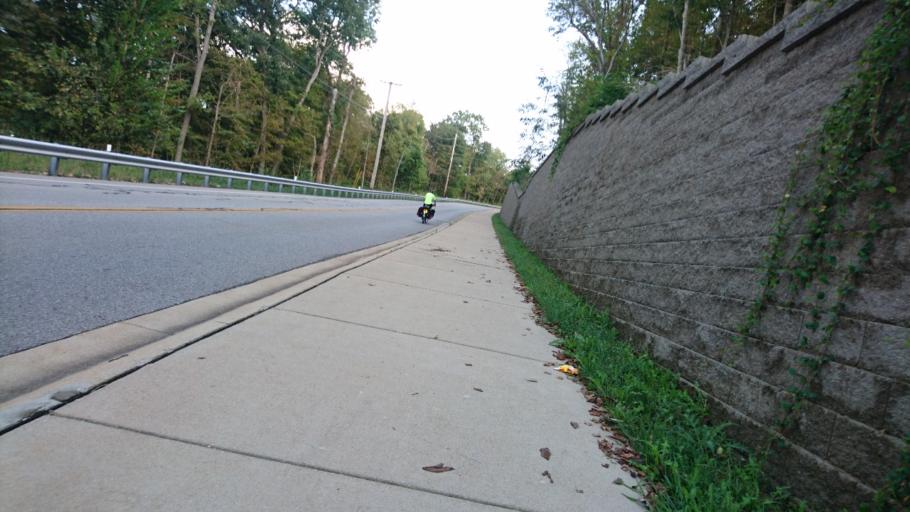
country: US
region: Missouri
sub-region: Saint Louis County
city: Eureka
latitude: 38.5145
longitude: -90.6338
